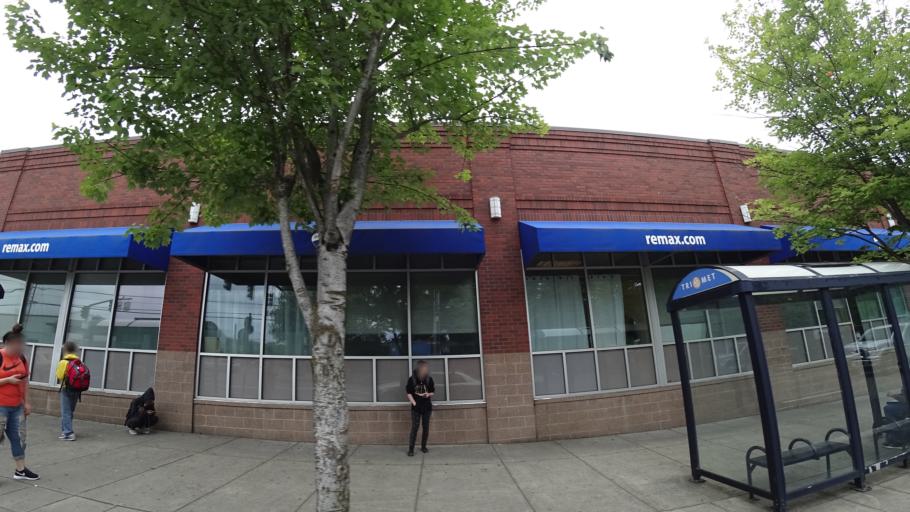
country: US
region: Oregon
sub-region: Multnomah County
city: Portland
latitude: 45.4789
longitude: -122.6931
